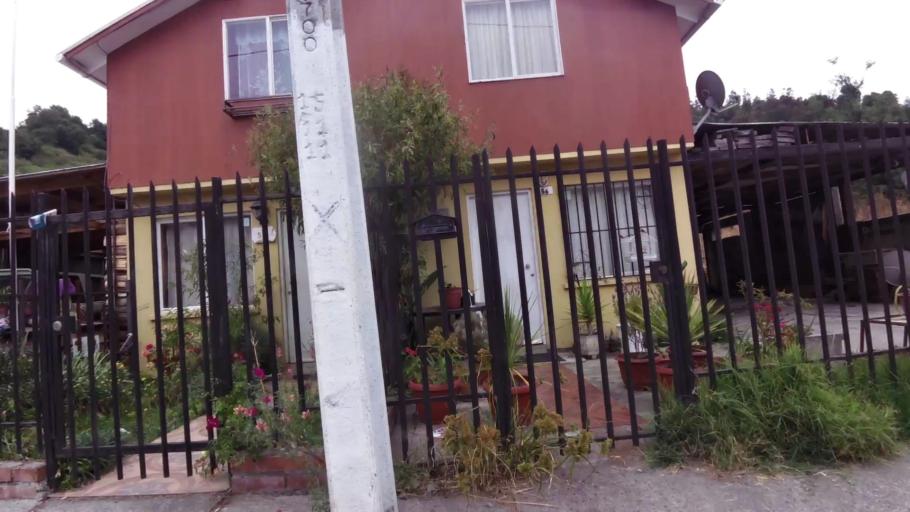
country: CL
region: Biobio
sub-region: Provincia de Concepcion
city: Concepcion
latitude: -36.8346
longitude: -73.0114
